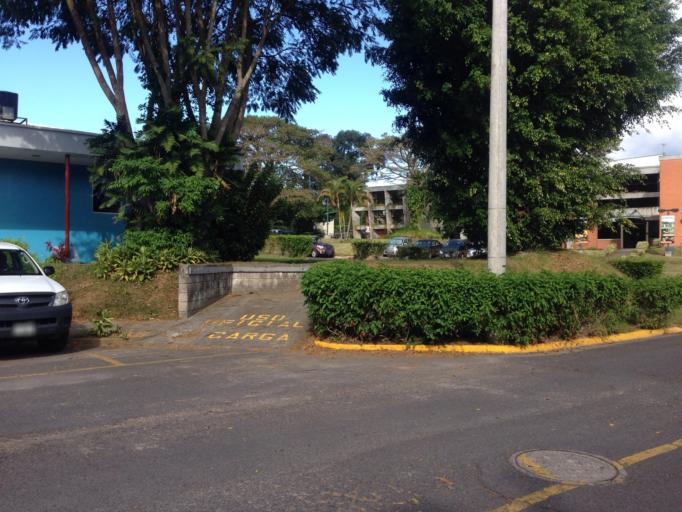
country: CR
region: San Jose
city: Sabanilla
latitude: 9.9400
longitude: -84.0438
